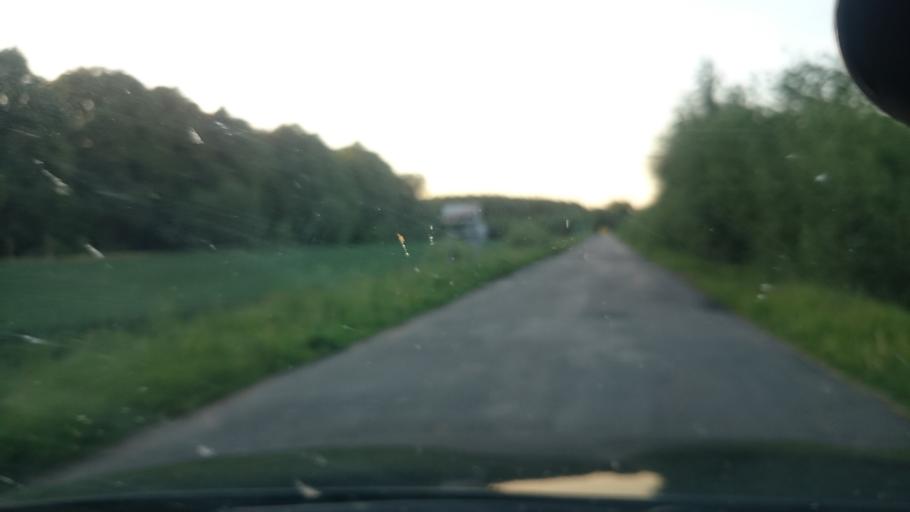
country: PL
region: Lower Silesian Voivodeship
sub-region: Powiat zabkowicki
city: Zloty Stok
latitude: 50.4758
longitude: 16.8469
